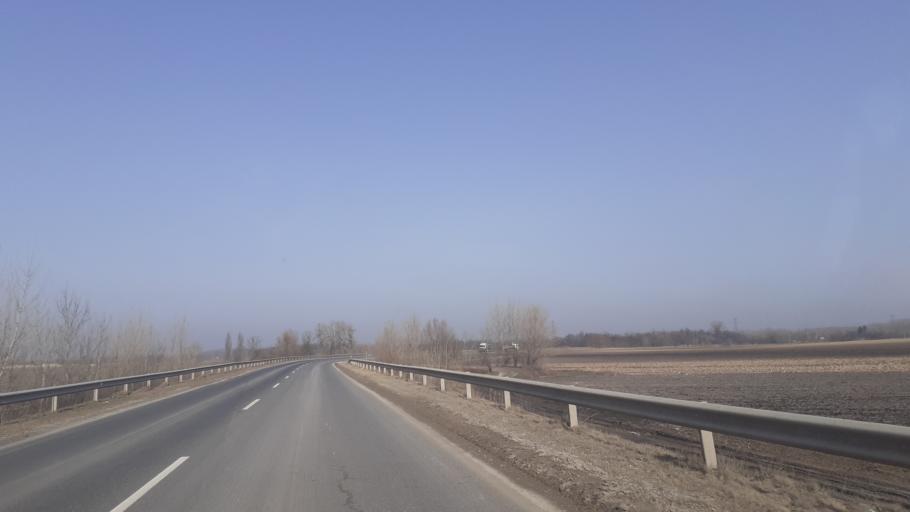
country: HU
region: Pest
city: Bugyi
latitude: 47.2380
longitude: 19.1209
